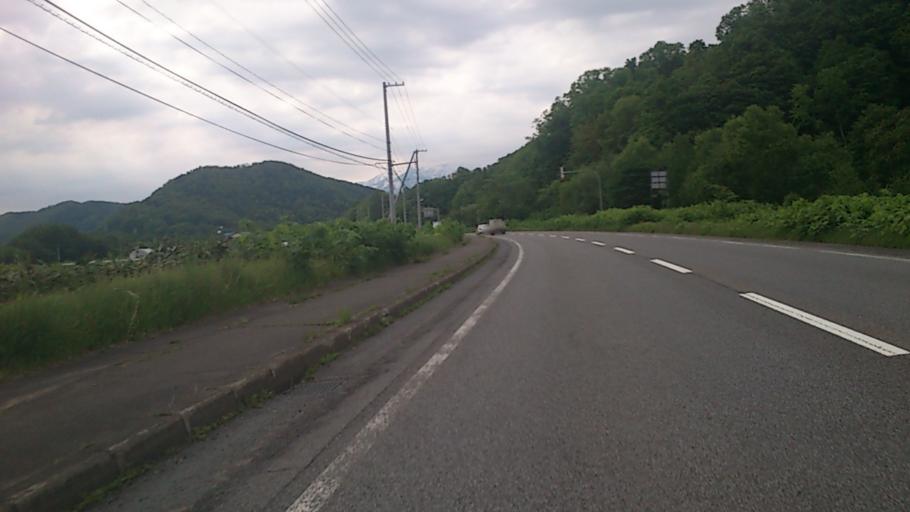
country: JP
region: Hokkaido
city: Kamikawa
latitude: 43.8475
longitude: 142.6960
